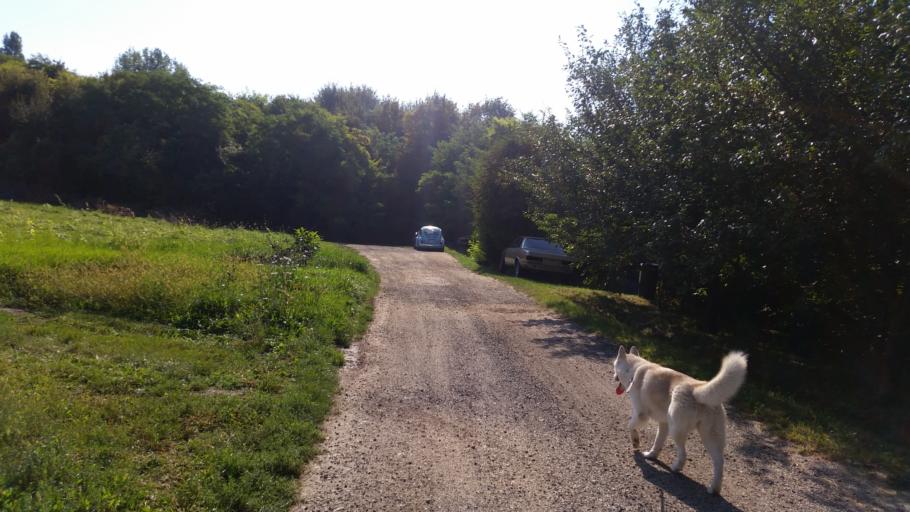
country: HU
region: Pest
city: Telki
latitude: 47.5461
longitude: 18.8373
